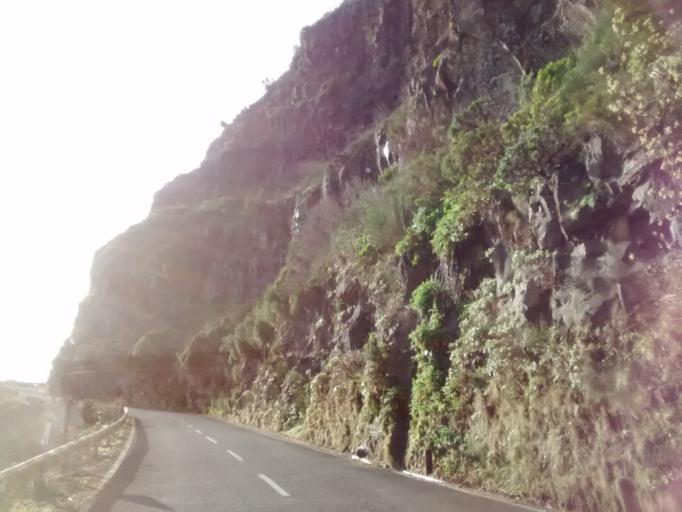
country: PT
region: Madeira
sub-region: Sao Vicente
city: Sao Vicente
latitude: 32.7381
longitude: -17.0504
